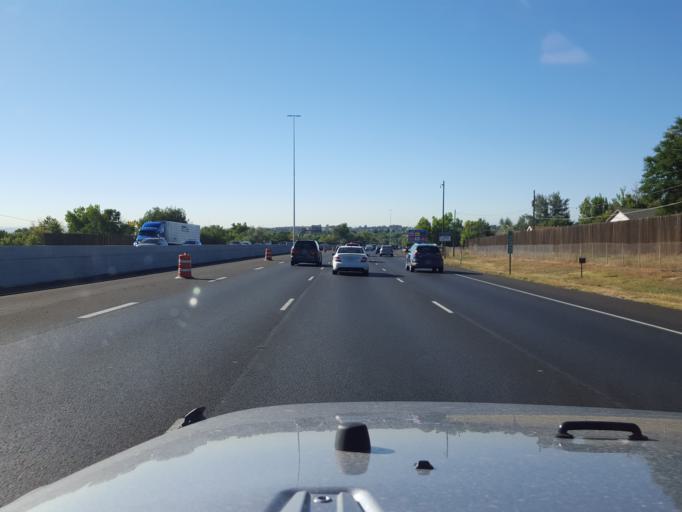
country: US
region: Colorado
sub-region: Adams County
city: Northglenn
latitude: 39.8997
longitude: -104.9880
